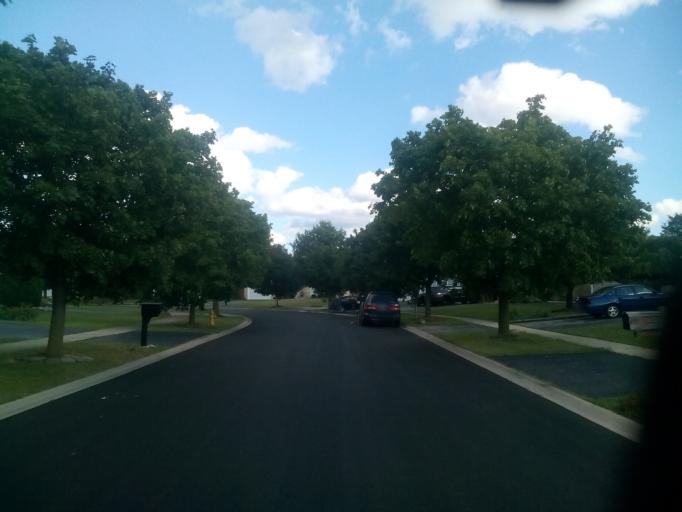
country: US
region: Illinois
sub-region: Will County
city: Romeoville
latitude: 41.6979
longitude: -88.1457
